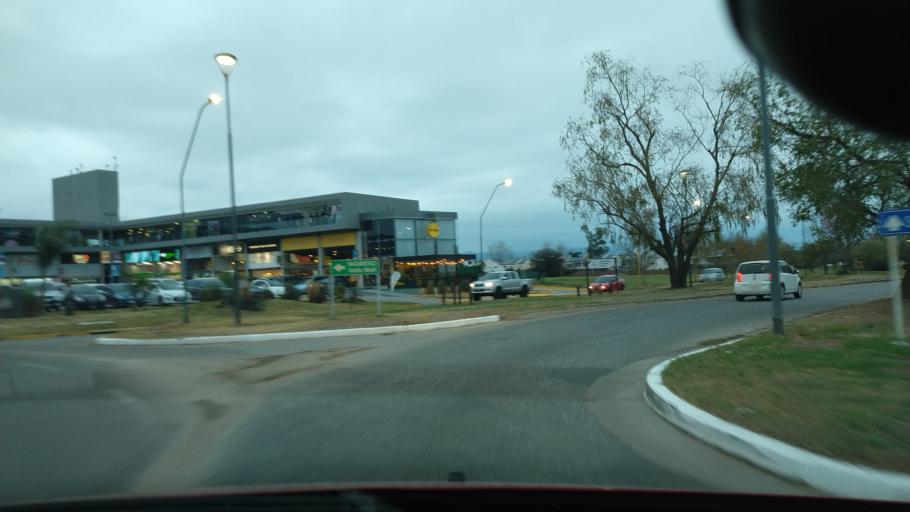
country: AR
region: Cordoba
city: La Calera
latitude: -31.3782
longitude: -64.2767
